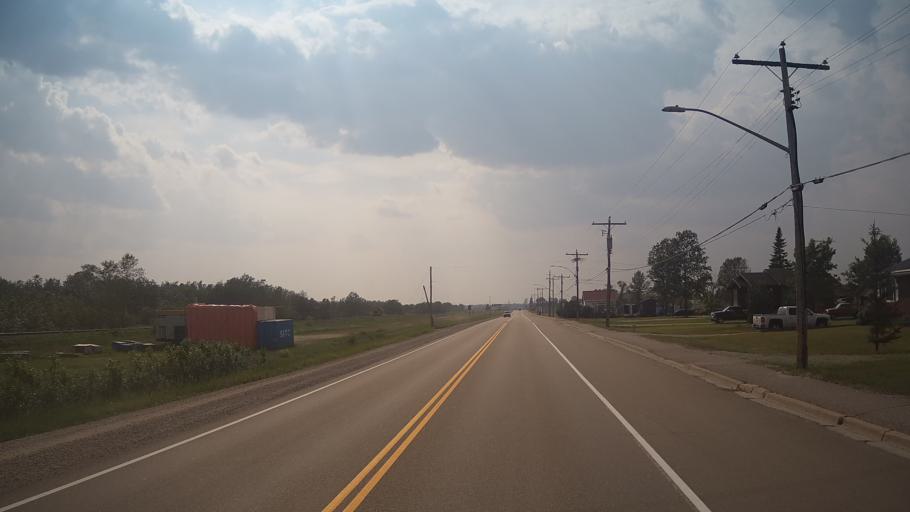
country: CA
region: Ontario
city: Kapuskasing
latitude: 49.5252
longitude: -82.8523
